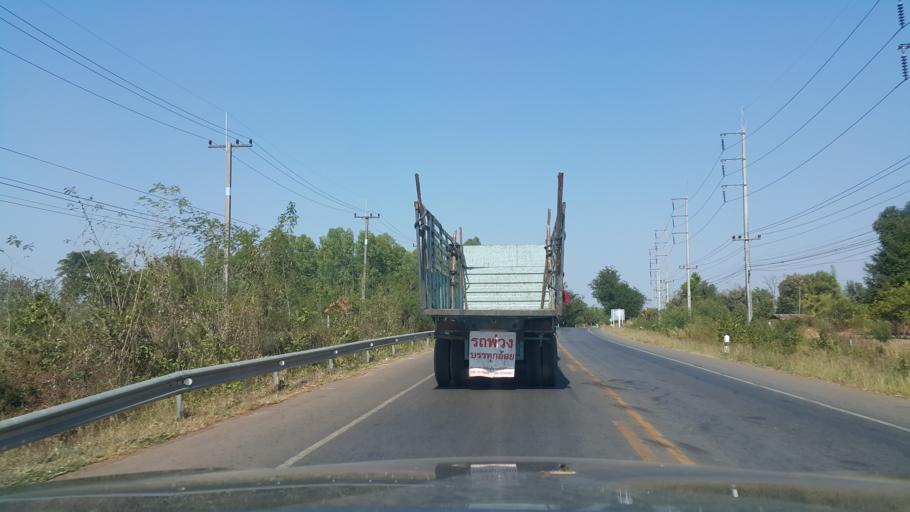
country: TH
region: Changwat Udon Thani
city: Nong Han
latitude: 17.4079
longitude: 103.1857
